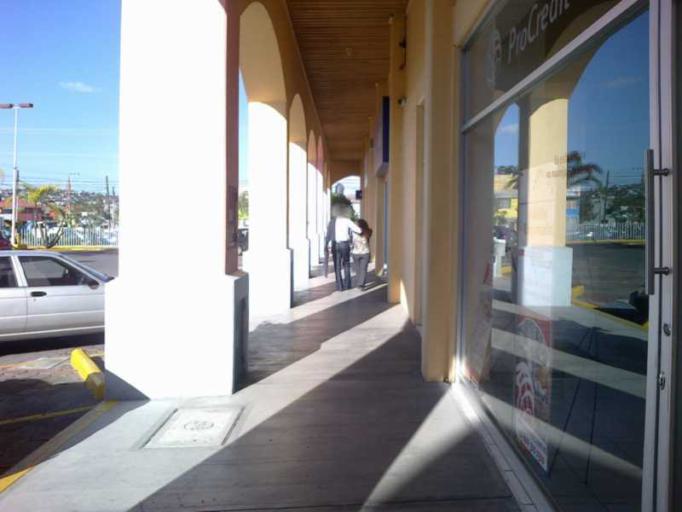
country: MX
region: Queretaro
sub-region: Queretaro
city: Sergio Villasenor
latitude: 20.6268
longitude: -100.4070
